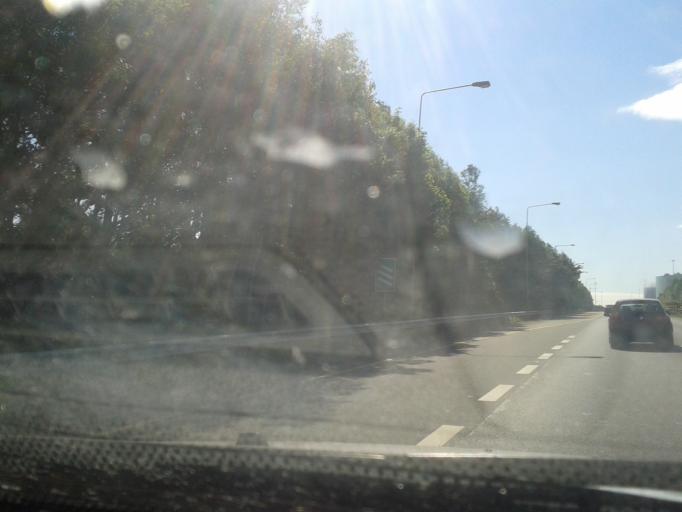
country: IE
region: Leinster
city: Hartstown
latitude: 53.4024
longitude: -6.4006
